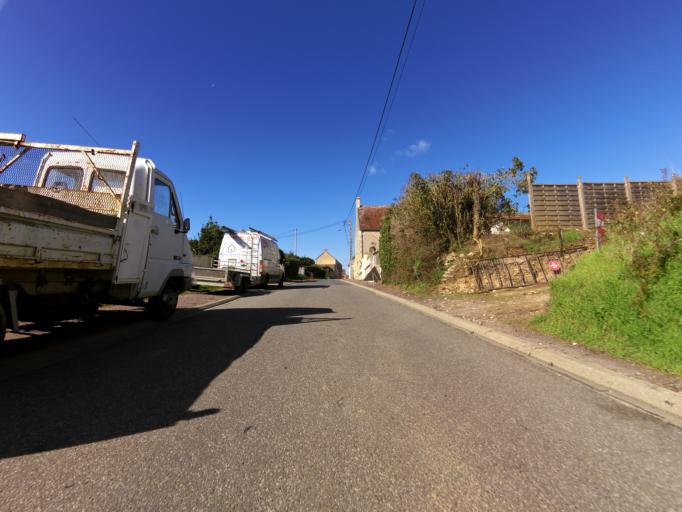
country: FR
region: Lower Normandy
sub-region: Departement du Calvados
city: Canon
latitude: 49.0469
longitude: -0.1283
